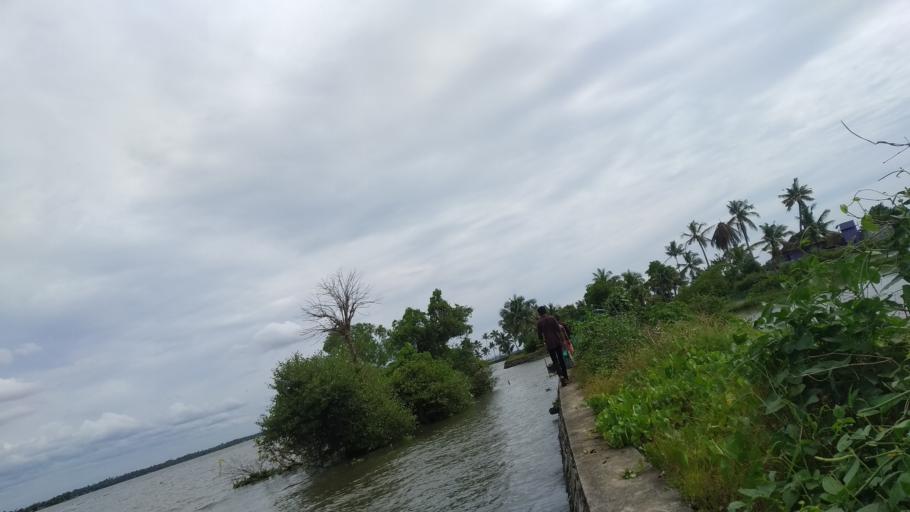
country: IN
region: Kerala
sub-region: Ernakulam
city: Elur
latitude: 10.0837
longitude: 76.2235
